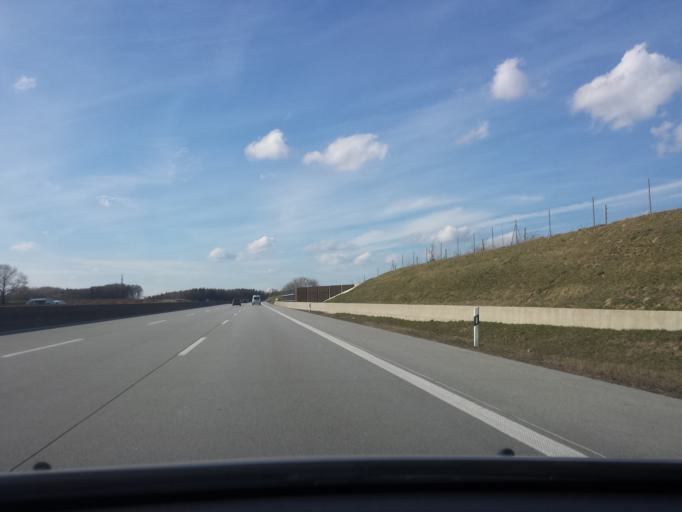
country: DE
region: Bavaria
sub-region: Upper Bavaria
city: Sulzemoos
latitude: 48.2699
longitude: 11.2886
